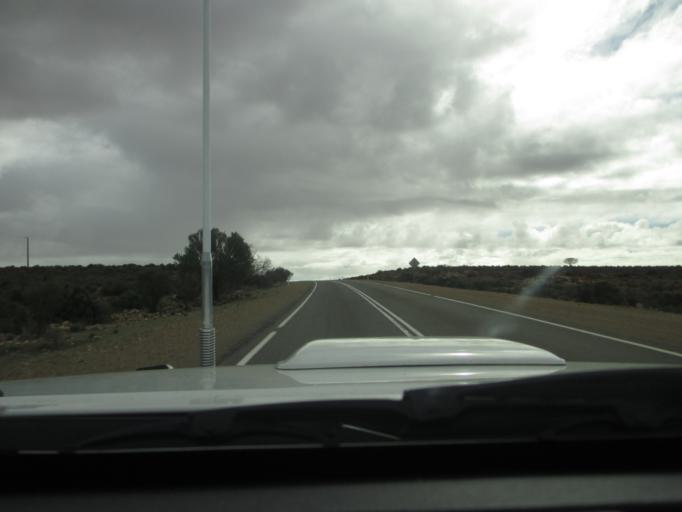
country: AU
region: South Australia
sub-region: Flinders Ranges
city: Quorn
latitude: -31.5601
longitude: 138.4289
